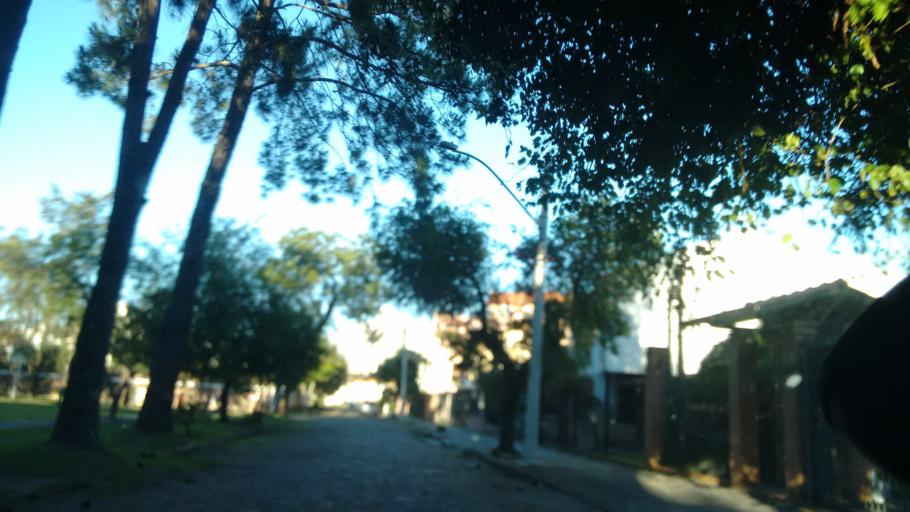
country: BR
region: Rio Grande do Sul
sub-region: Cachoeirinha
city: Cachoeirinha
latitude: -30.0049
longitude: -51.1471
